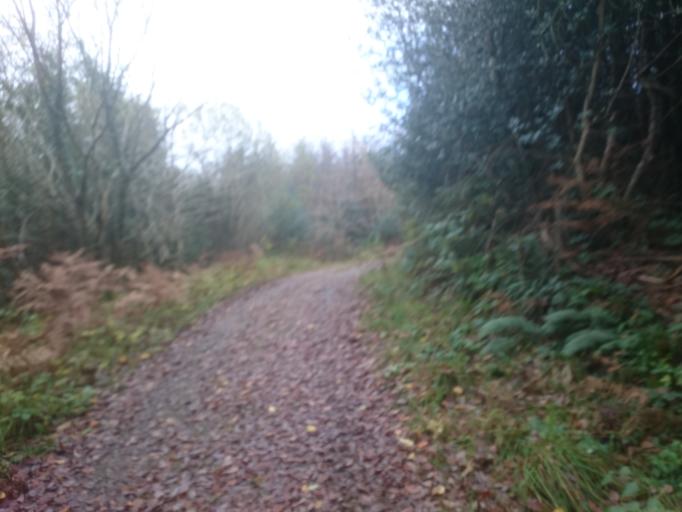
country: IE
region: Leinster
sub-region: Kilkenny
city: Thomastown
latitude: 52.4677
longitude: -7.0503
